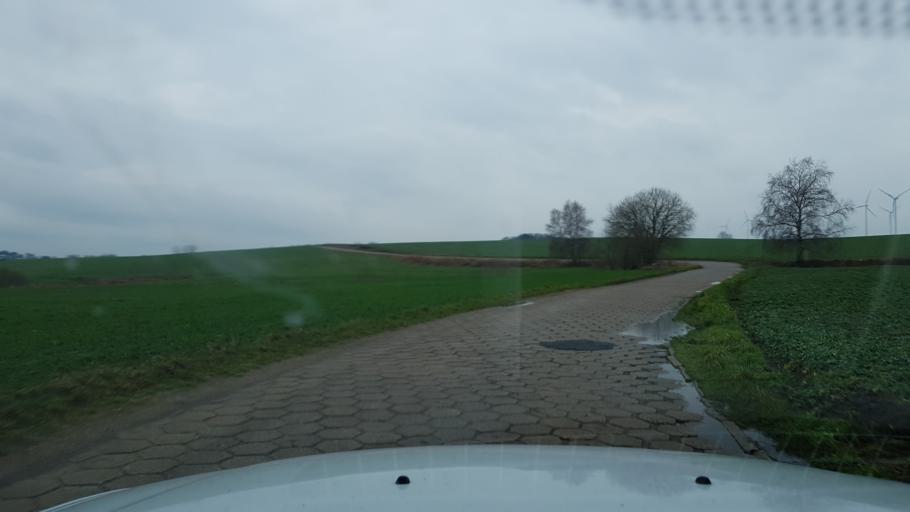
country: PL
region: West Pomeranian Voivodeship
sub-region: Powiat kolobrzeski
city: Grzybowo
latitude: 54.1057
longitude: 15.4534
